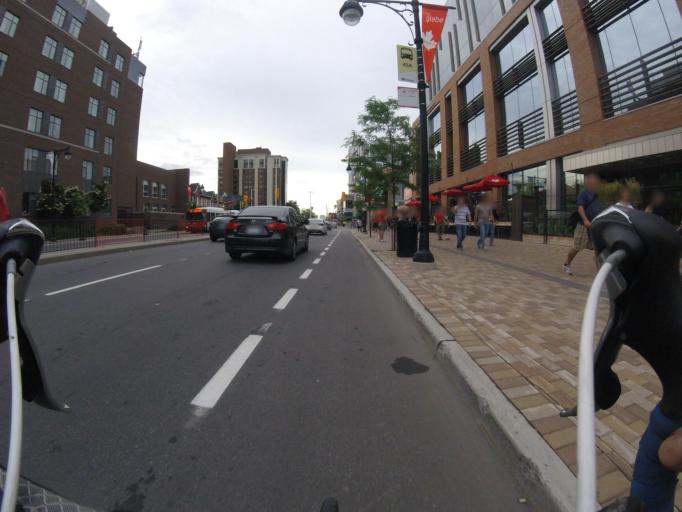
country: CA
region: Ontario
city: Ottawa
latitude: 45.3983
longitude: -75.6856
